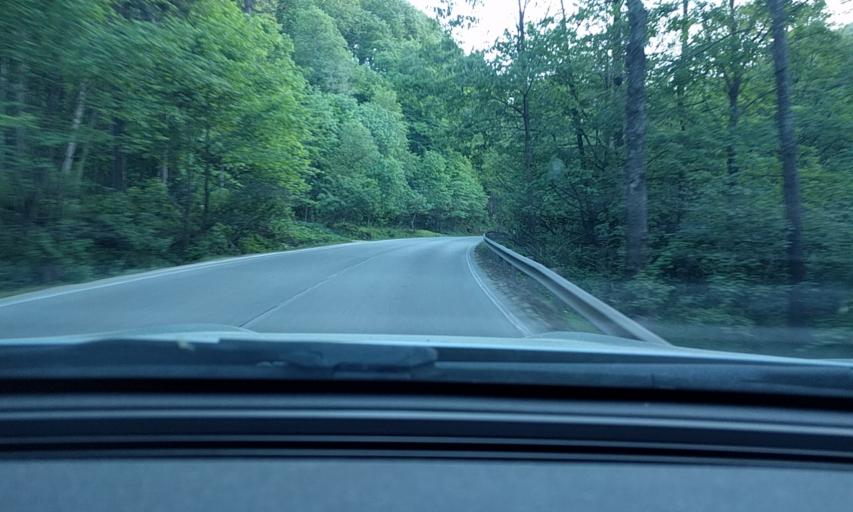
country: RO
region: Bacau
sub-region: Oras Slanic-Moldova
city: Slanic-Moldova
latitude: 46.1111
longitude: 26.4163
